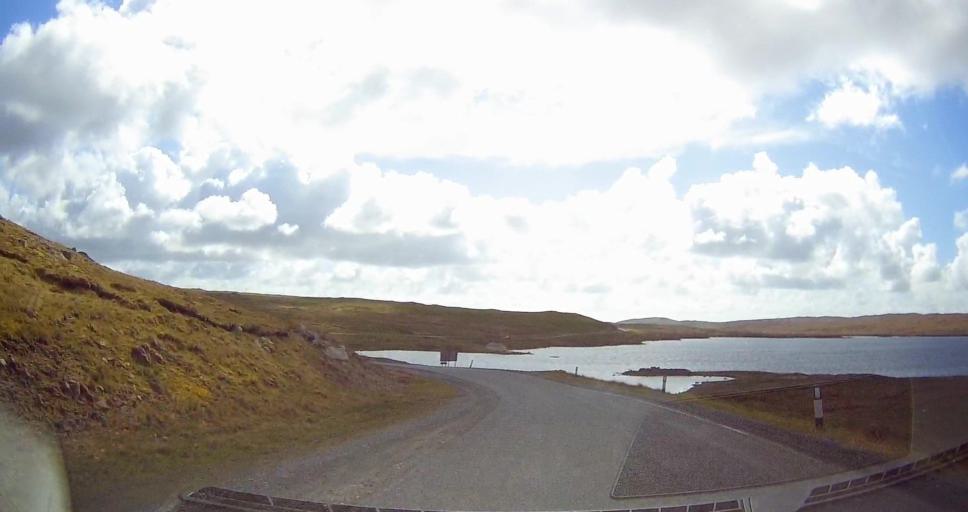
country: GB
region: Scotland
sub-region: Shetland Islands
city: Lerwick
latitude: 60.4896
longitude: -1.3895
